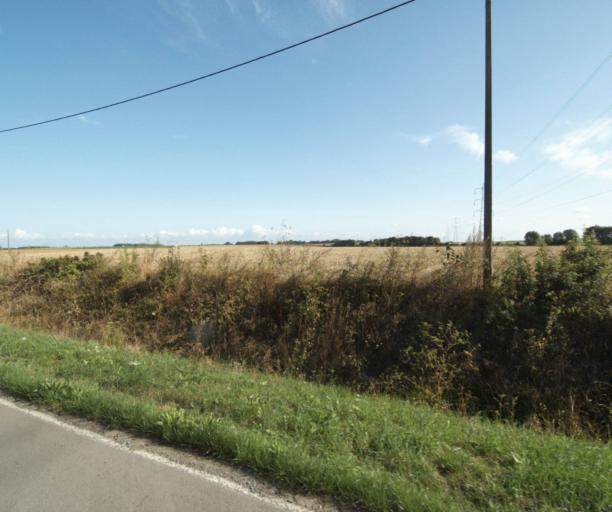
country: FR
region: Nord-Pas-de-Calais
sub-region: Departement du Nord
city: Cysoing
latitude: 50.5753
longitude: 3.1993
